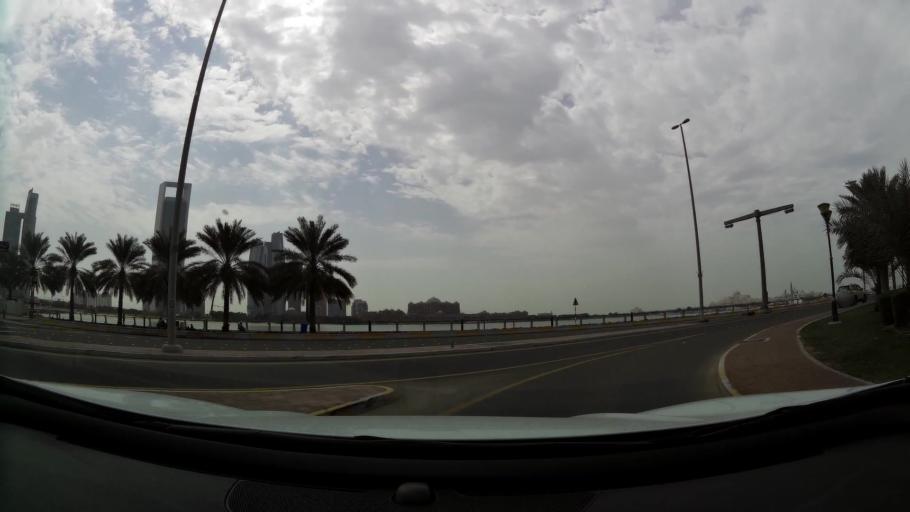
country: AE
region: Abu Dhabi
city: Abu Dhabi
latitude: 24.4721
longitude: 54.3199
